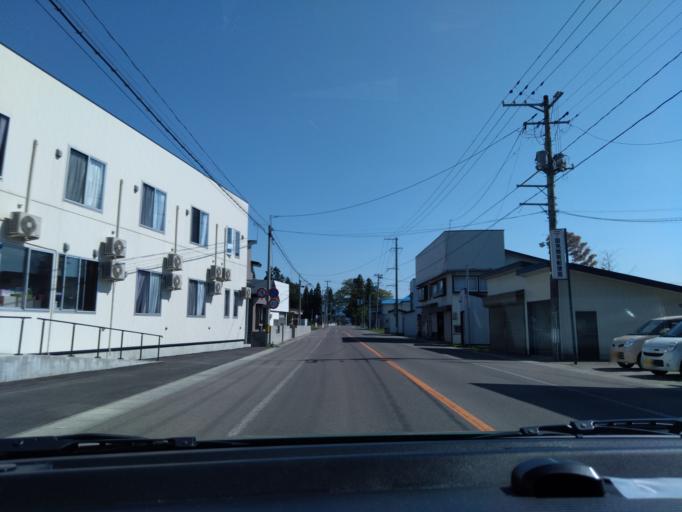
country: JP
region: Akita
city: Kakunodatemachi
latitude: 39.5308
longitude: 140.5857
